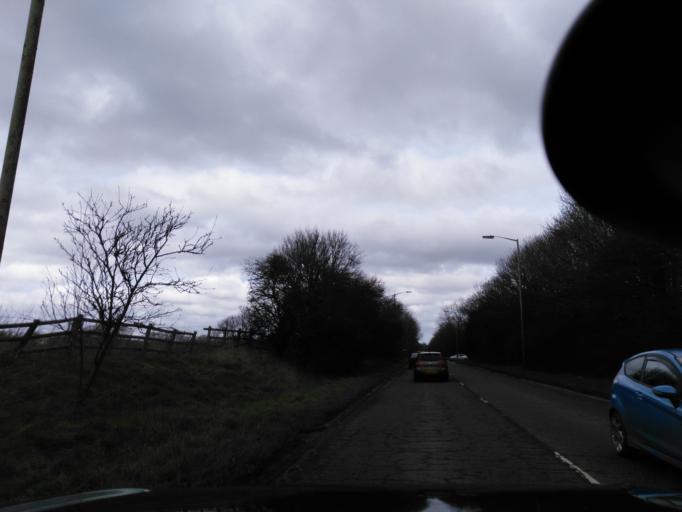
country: GB
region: England
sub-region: Wiltshire
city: Melksham
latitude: 51.3702
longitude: -2.1454
